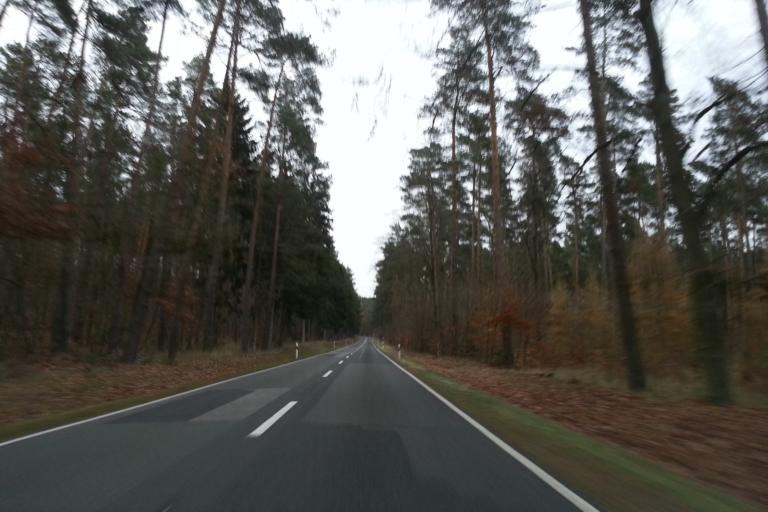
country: DE
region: Mecklenburg-Vorpommern
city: Ferdinandshof
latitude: 53.5954
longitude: 13.8449
